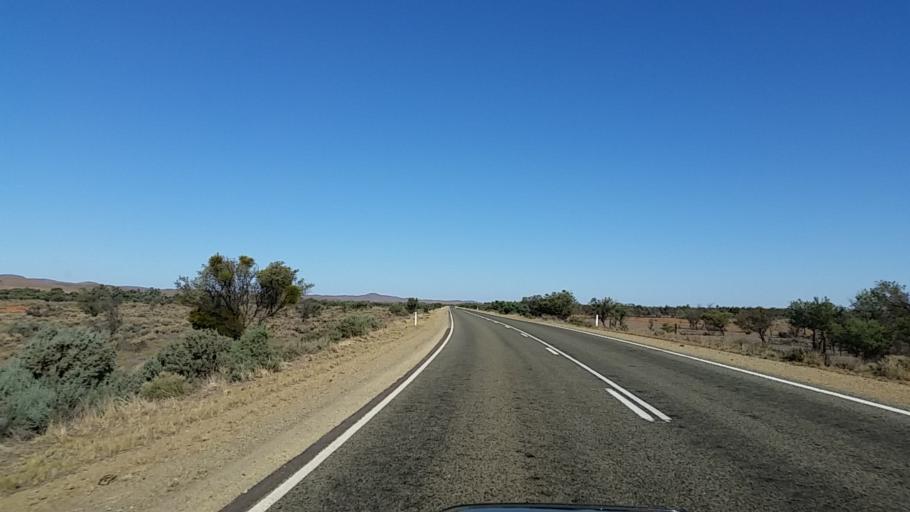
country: AU
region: South Australia
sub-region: Flinders Ranges
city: Quorn
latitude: -32.3870
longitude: 138.5038
